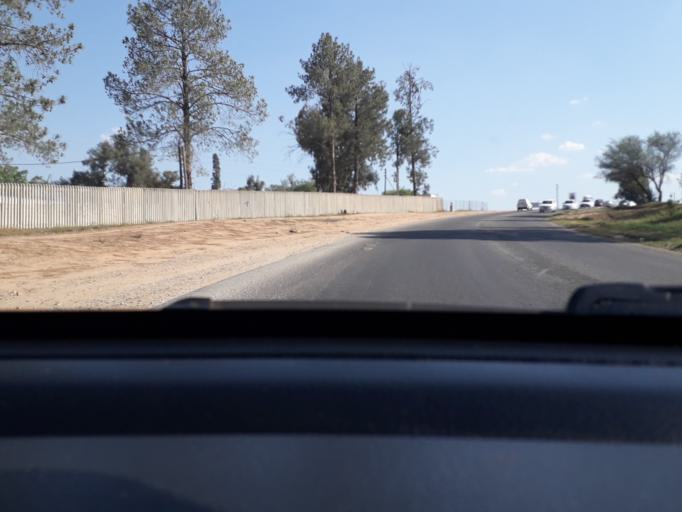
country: ZA
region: Gauteng
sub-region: City of Johannesburg Metropolitan Municipality
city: Midrand
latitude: -26.0332
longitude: 28.1114
